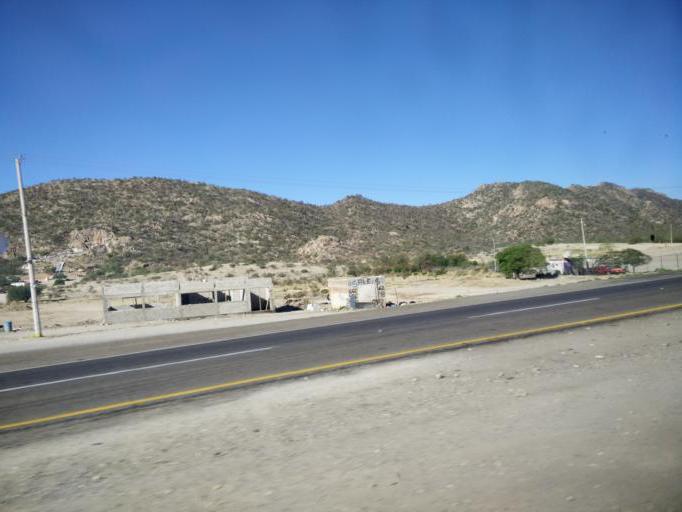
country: MX
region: Sonora
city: Hermosillo
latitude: 28.9862
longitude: -110.9693
